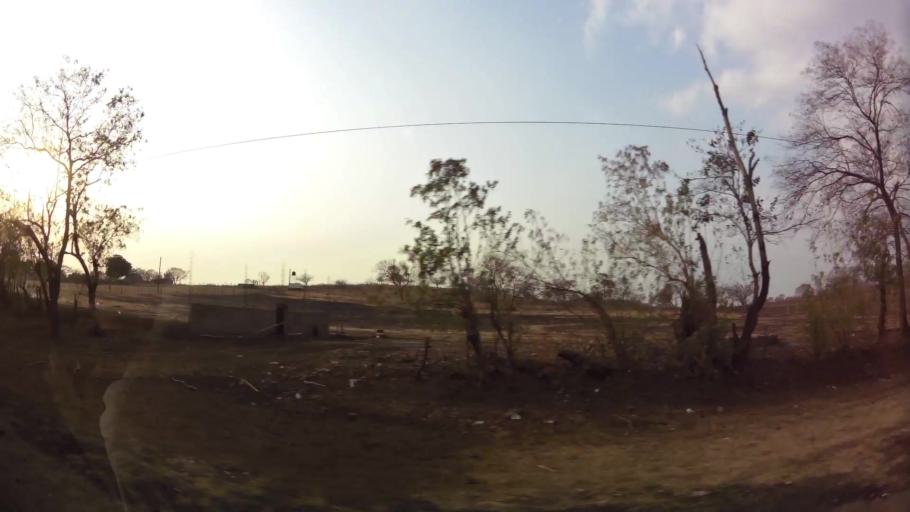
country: NI
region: Leon
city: Nagarote
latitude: 12.2693
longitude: -86.5408
